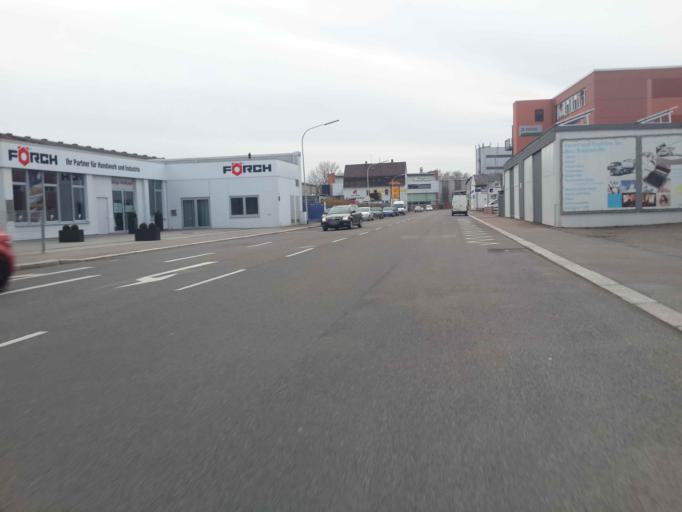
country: DE
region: Baden-Wuerttemberg
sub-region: Regierungsbezirk Stuttgart
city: Heilbronn
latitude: 49.1595
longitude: 9.2186
